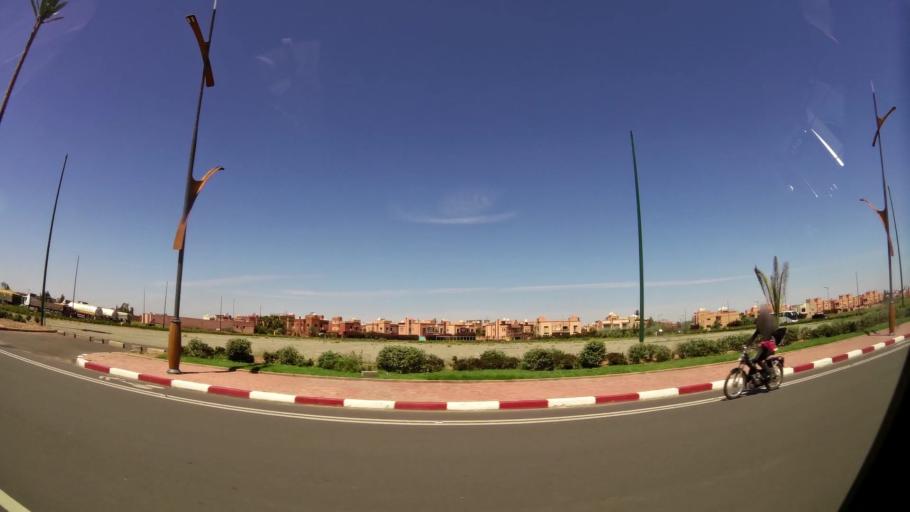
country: MA
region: Marrakech-Tensift-Al Haouz
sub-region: Marrakech
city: Marrakesh
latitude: 31.6083
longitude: -7.9962
